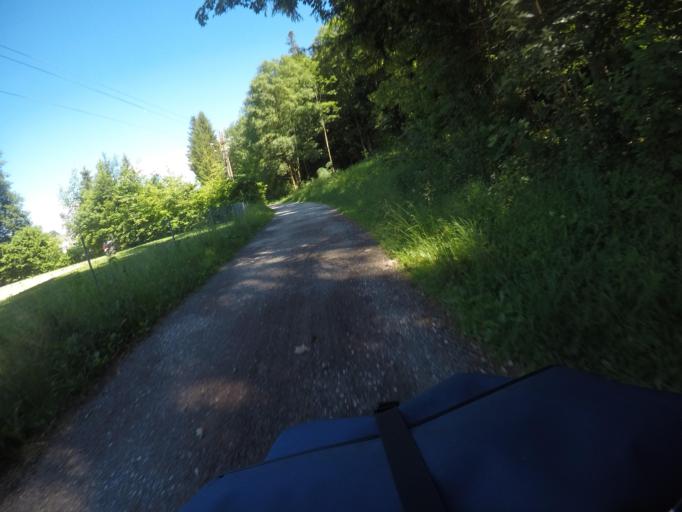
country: DE
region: Bavaria
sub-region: Swabia
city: Fuessen
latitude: 47.5671
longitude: 10.6718
